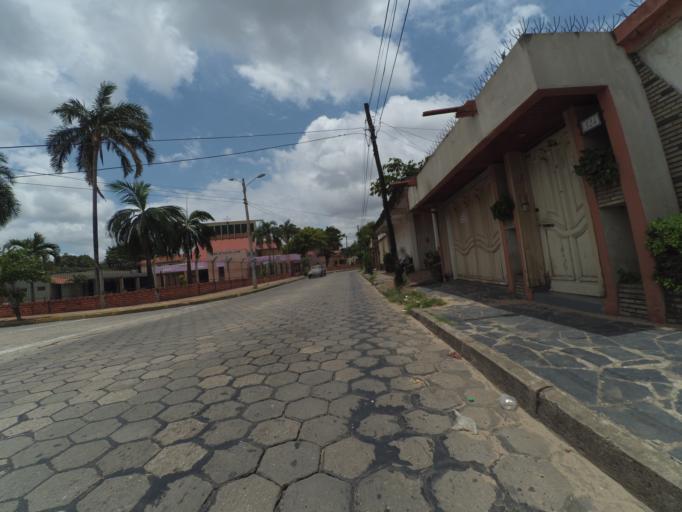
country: BO
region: Santa Cruz
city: Santa Cruz de la Sierra
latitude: -17.7978
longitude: -63.2007
